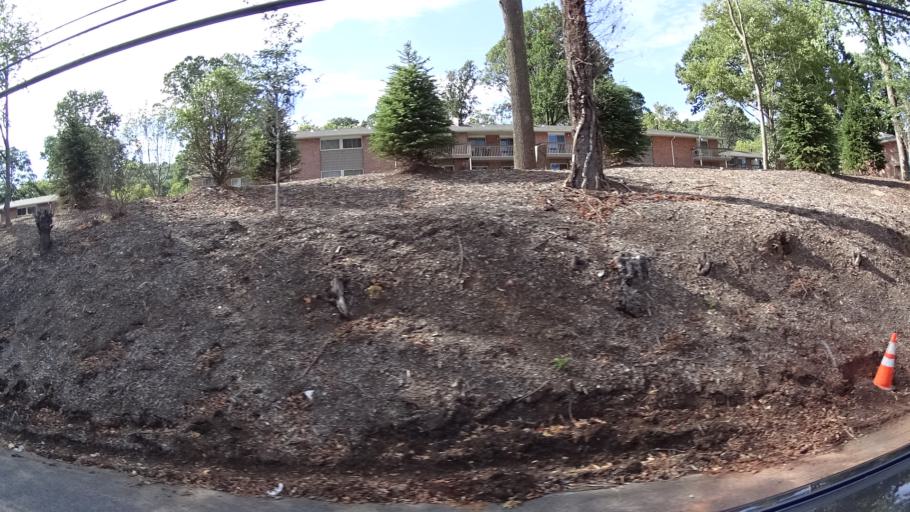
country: US
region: New Jersey
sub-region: Middlesex County
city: Dunellen
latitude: 40.6124
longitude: -74.4602
